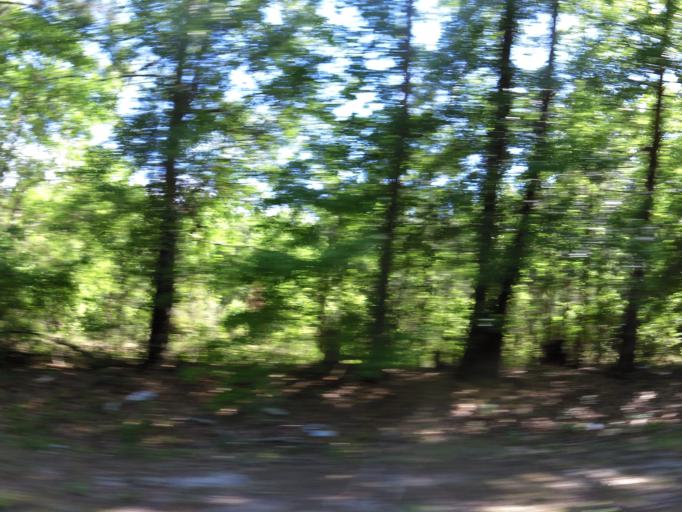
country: US
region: South Carolina
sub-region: Bamberg County
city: Denmark
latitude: 33.3450
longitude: -81.1995
